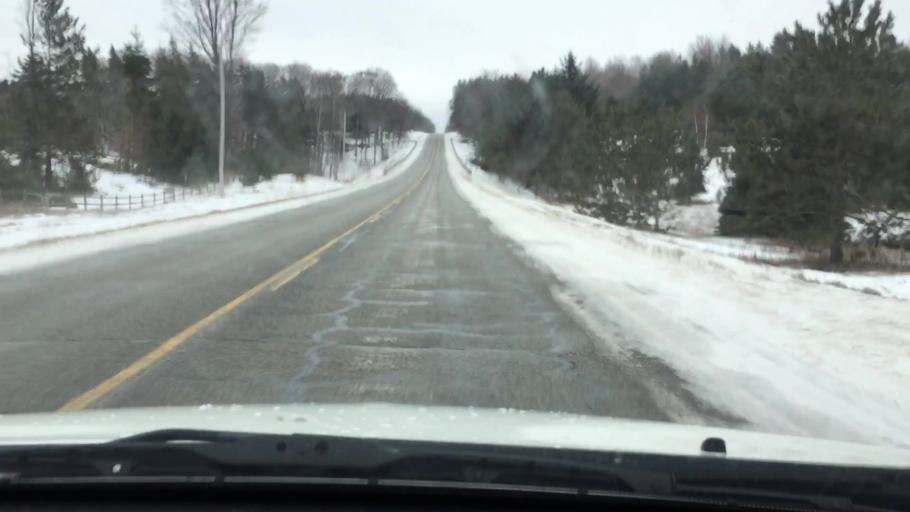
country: US
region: Michigan
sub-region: Wexford County
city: Cadillac
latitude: 44.1787
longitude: -85.4055
